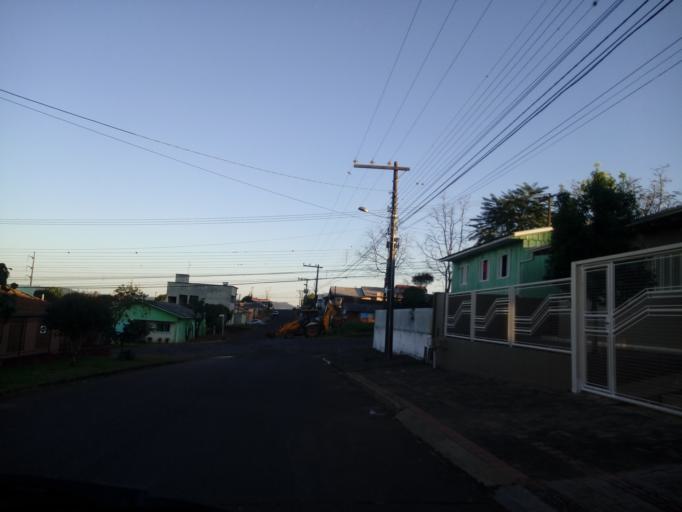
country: BR
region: Santa Catarina
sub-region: Chapeco
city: Chapeco
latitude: -27.0798
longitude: -52.6328
